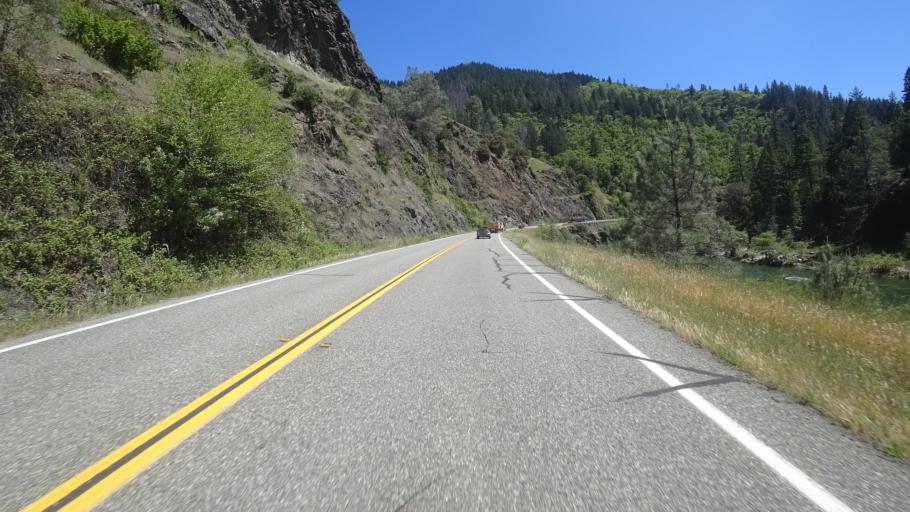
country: US
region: California
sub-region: Trinity County
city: Hayfork
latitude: 40.7620
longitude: -123.2843
